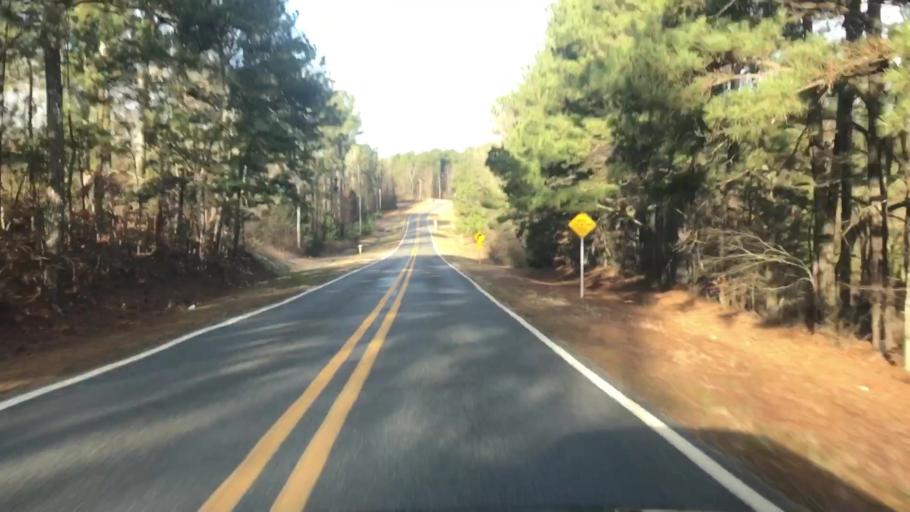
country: US
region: Arkansas
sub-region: Garland County
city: Rockwell
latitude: 34.4777
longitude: -93.2671
